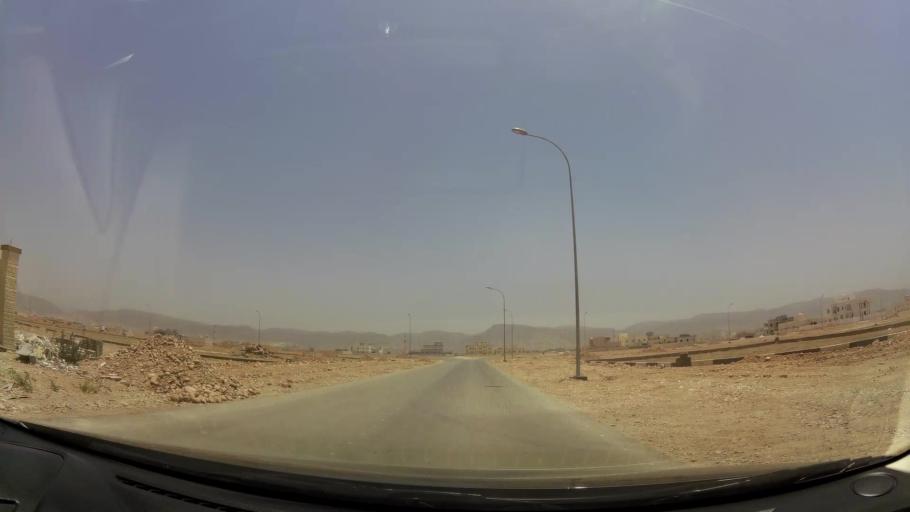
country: OM
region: Zufar
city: Salalah
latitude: 17.0969
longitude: 54.1838
